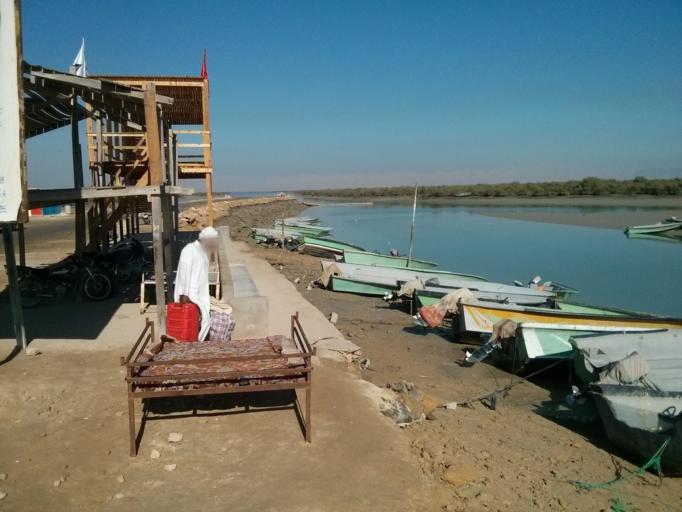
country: IR
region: Hormozgan
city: Bandar-e Khamir
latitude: 26.7854
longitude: 55.7649
